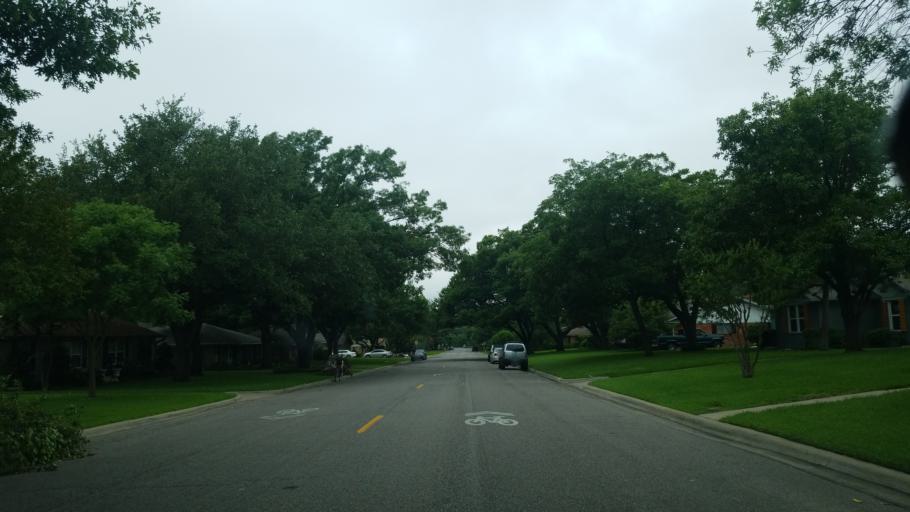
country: US
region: Texas
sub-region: Dallas County
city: Farmers Branch
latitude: 32.9023
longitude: -96.8583
